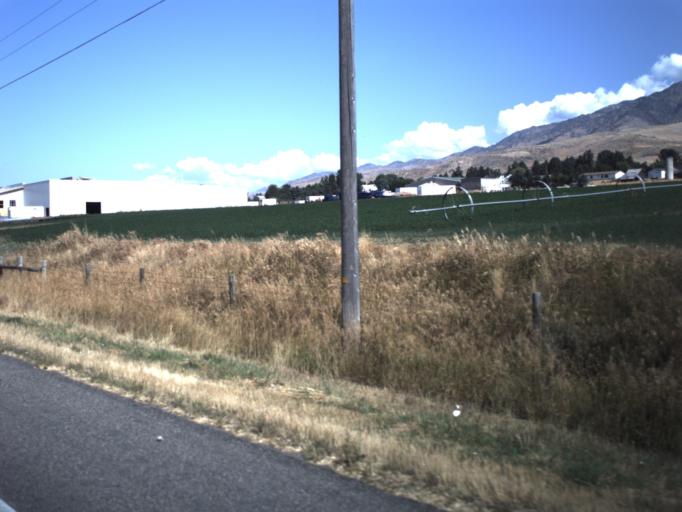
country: US
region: Utah
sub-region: Cache County
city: Richmond
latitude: 41.9040
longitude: -111.8147
